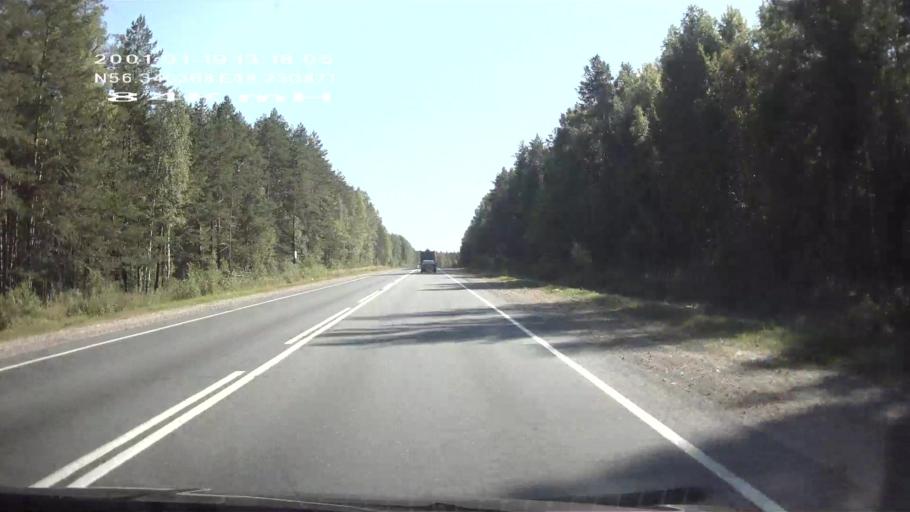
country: RU
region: Mariy-El
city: Suslonger
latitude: 56.3401
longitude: 48.2311
